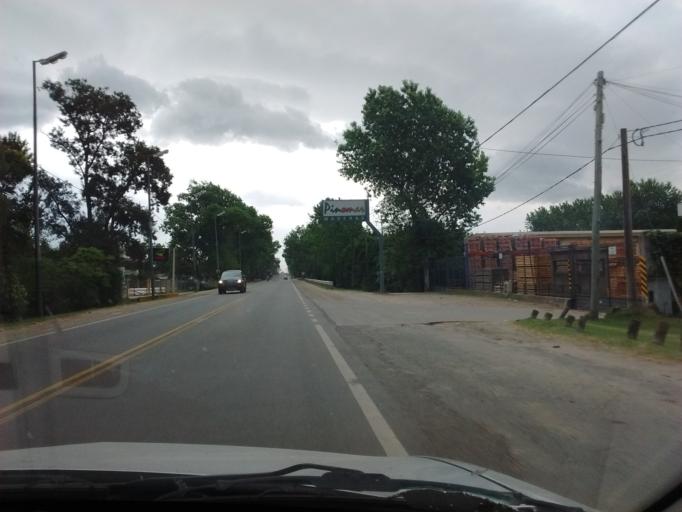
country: AR
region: Santa Fe
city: Funes
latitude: -32.9264
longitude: -60.7527
